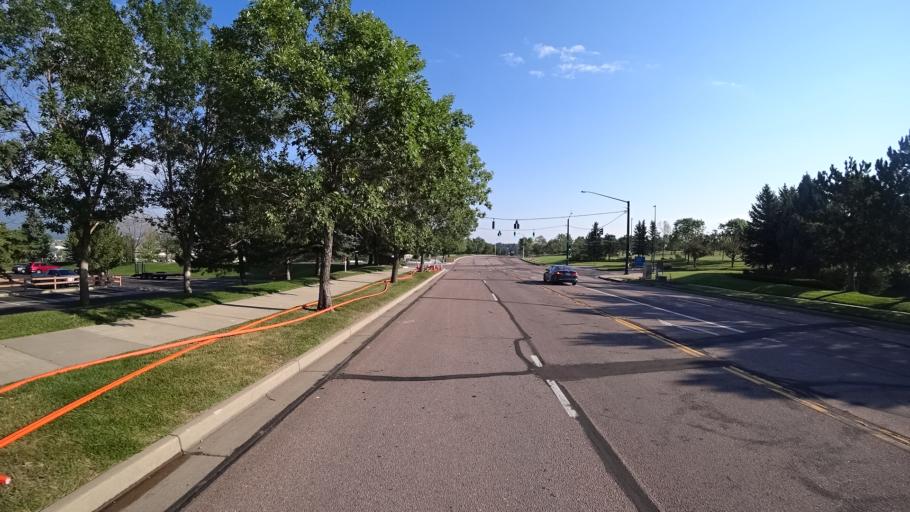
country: US
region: Colorado
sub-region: El Paso County
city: Air Force Academy
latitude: 38.9618
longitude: -104.7918
